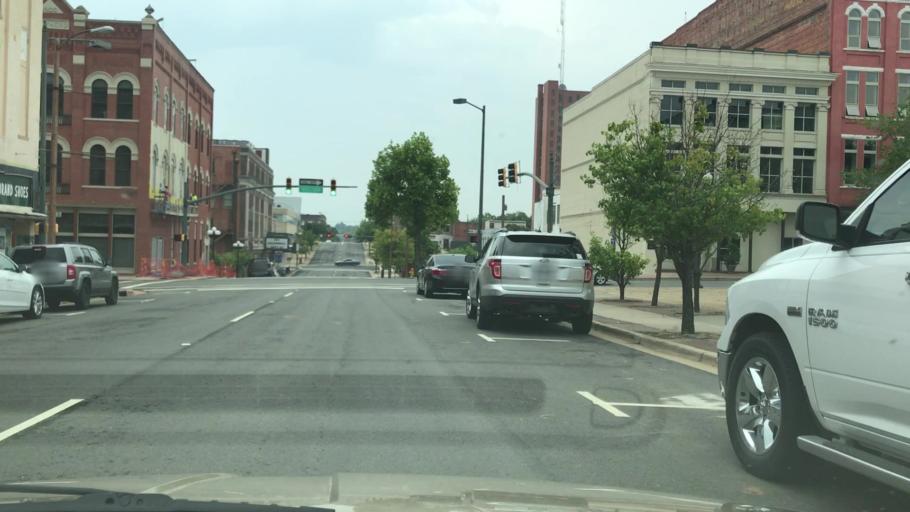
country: US
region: Louisiana
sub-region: Caddo Parish
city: Shreveport
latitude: 32.5110
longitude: -93.7511
